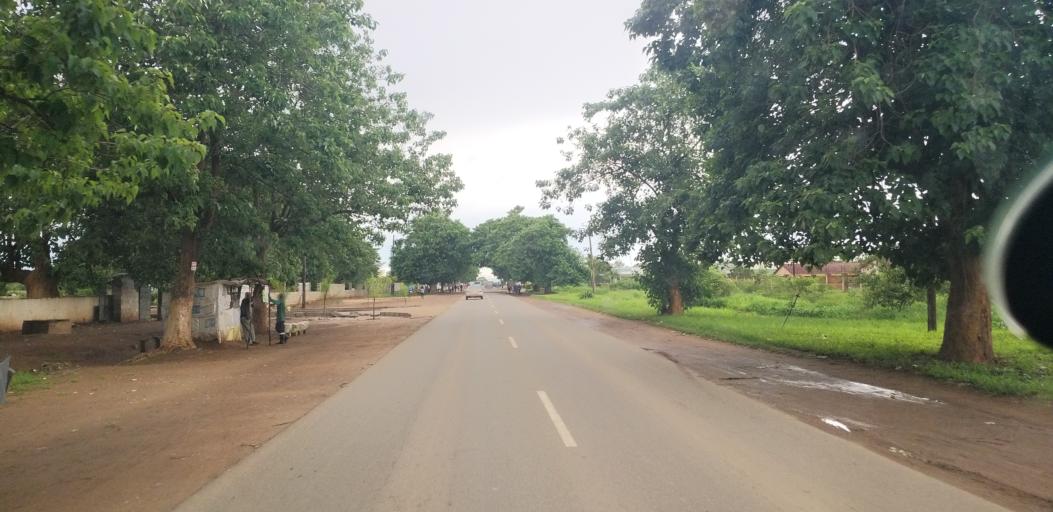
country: ZM
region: Lusaka
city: Lusaka
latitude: -15.4386
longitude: 28.3592
